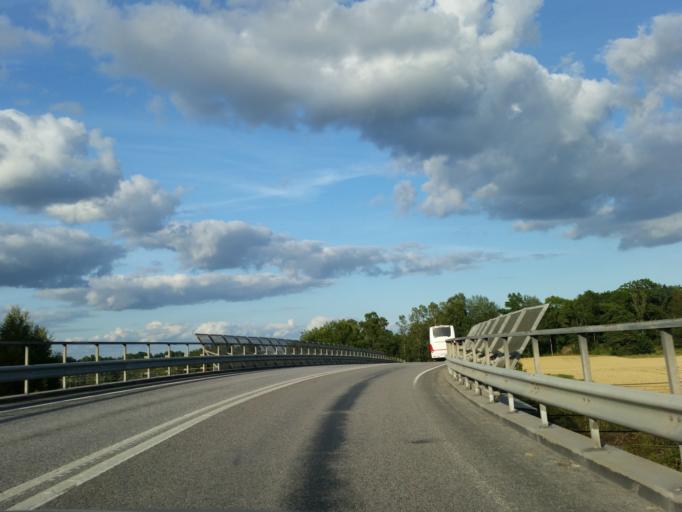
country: SE
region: Stockholm
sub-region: Sodertalje Kommun
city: Molnbo
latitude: 59.0791
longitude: 17.5441
